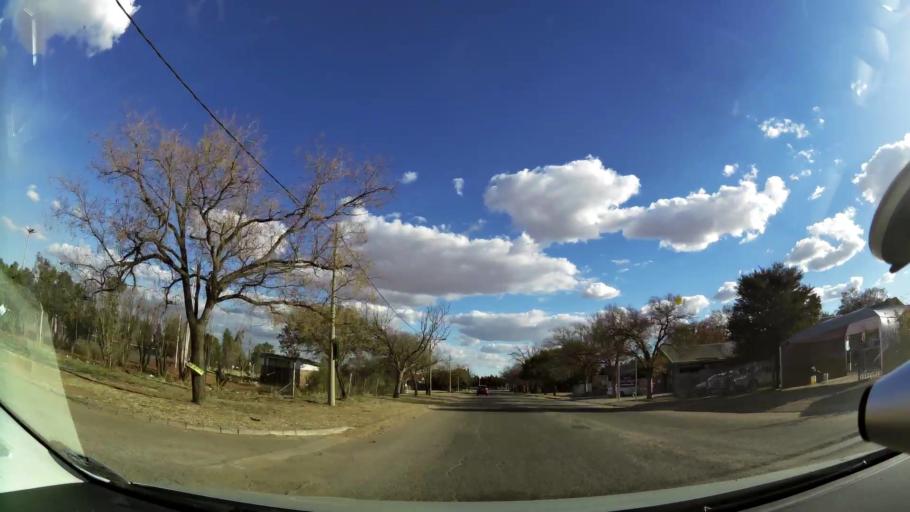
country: ZA
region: North-West
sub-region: Dr Kenneth Kaunda District Municipality
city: Klerksdorp
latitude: -26.8444
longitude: 26.6638
